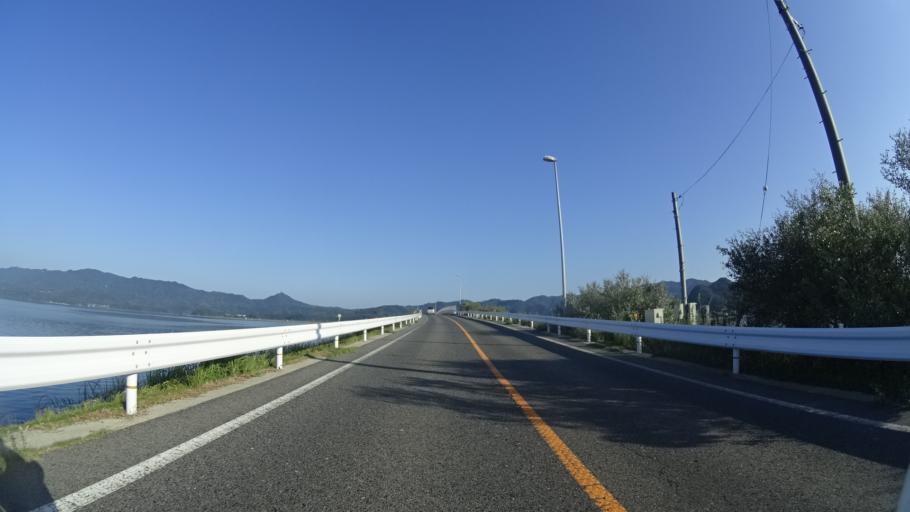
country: JP
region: Shimane
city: Sakaiminato
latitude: 35.5193
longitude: 133.1830
